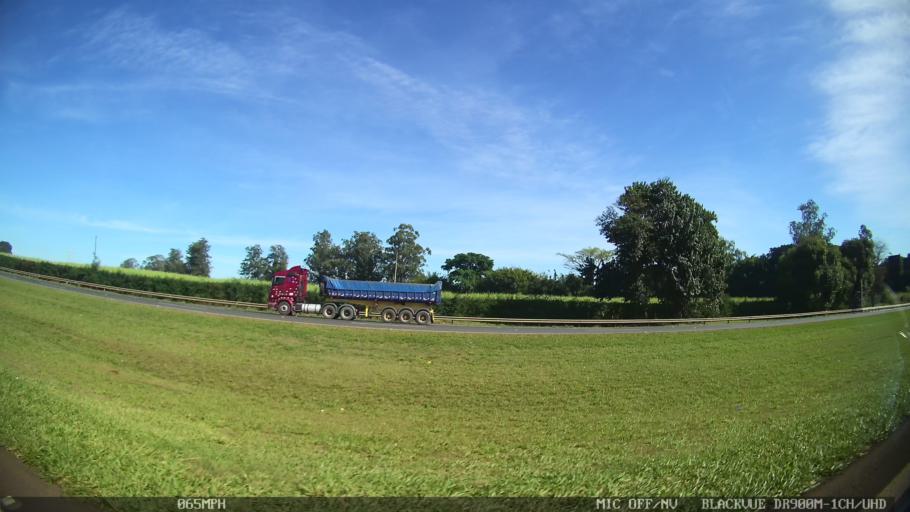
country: BR
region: Sao Paulo
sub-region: Leme
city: Leme
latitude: -22.2388
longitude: -47.3908
